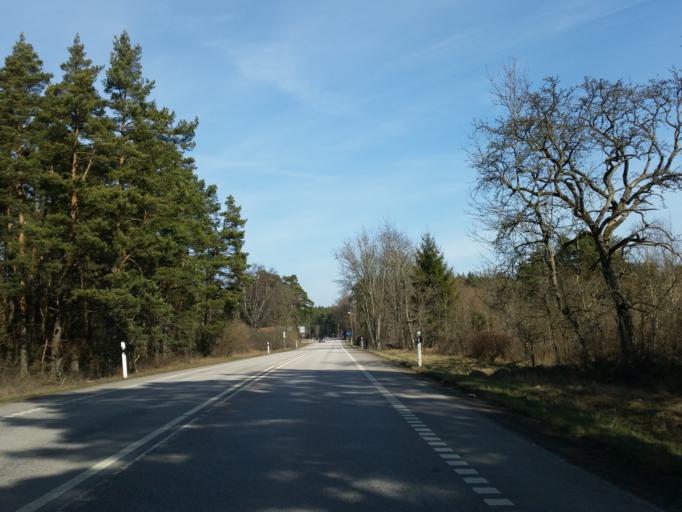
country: SE
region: Kalmar
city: Faerjestaden
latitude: 56.7524
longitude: 16.5512
